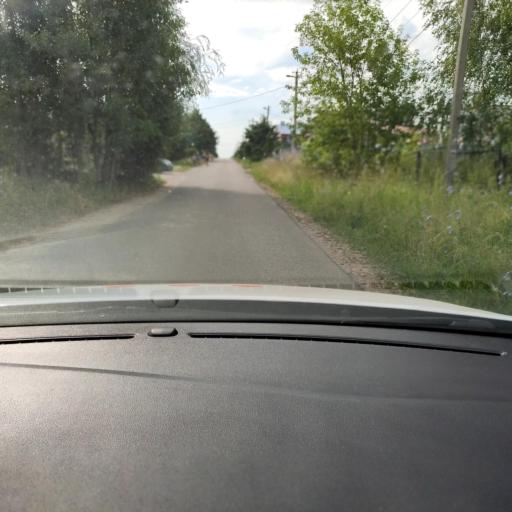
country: RU
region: Tatarstan
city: Stolbishchi
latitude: 55.7595
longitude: 49.2846
